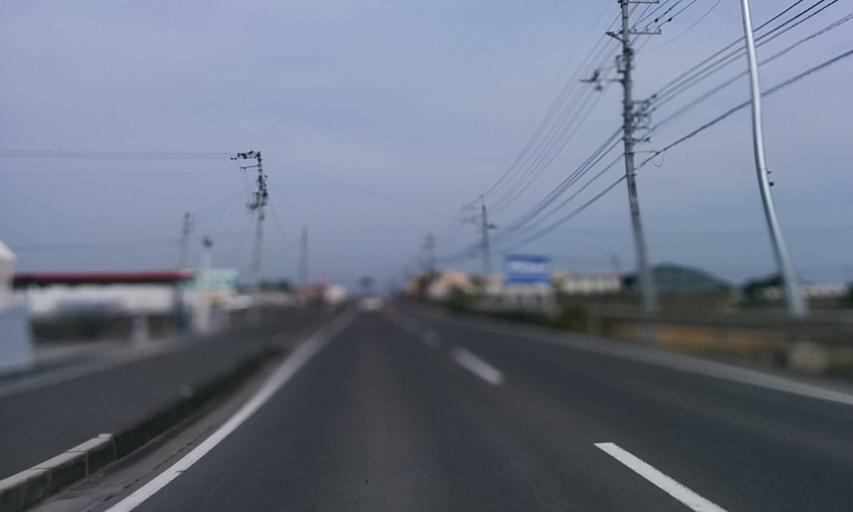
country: JP
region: Ehime
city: Kawanoecho
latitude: 33.9670
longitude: 133.4869
